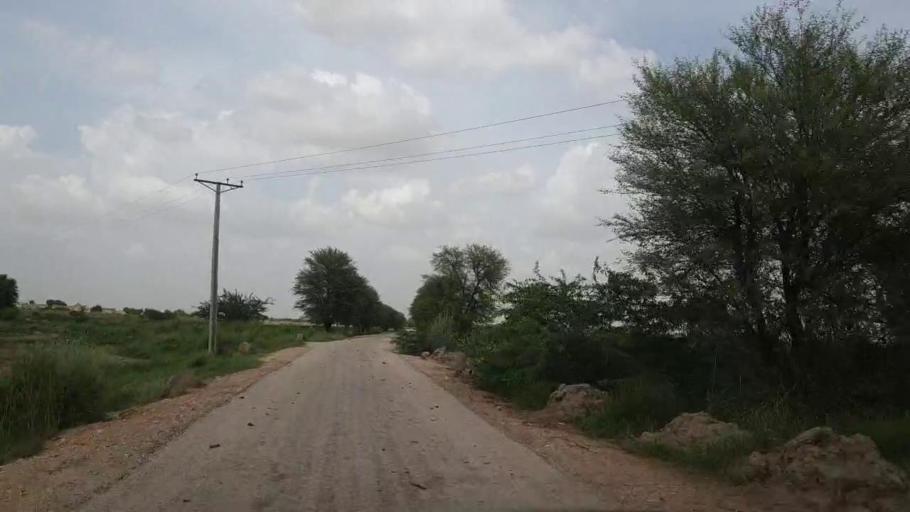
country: PK
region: Sindh
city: Kot Diji
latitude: 27.2247
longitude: 69.0863
